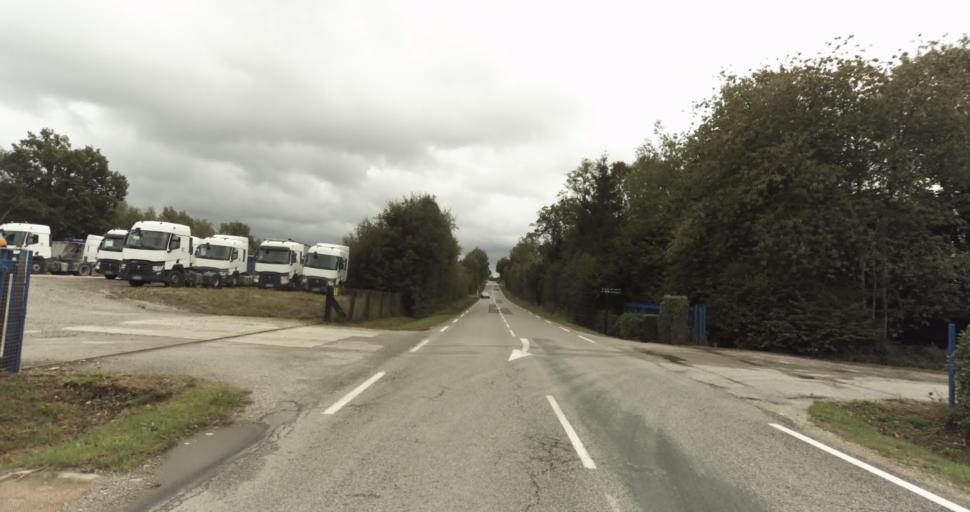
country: FR
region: Lower Normandy
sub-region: Departement de l'Orne
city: Sainte-Gauburge-Sainte-Colombe
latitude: 48.7034
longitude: 0.4380
